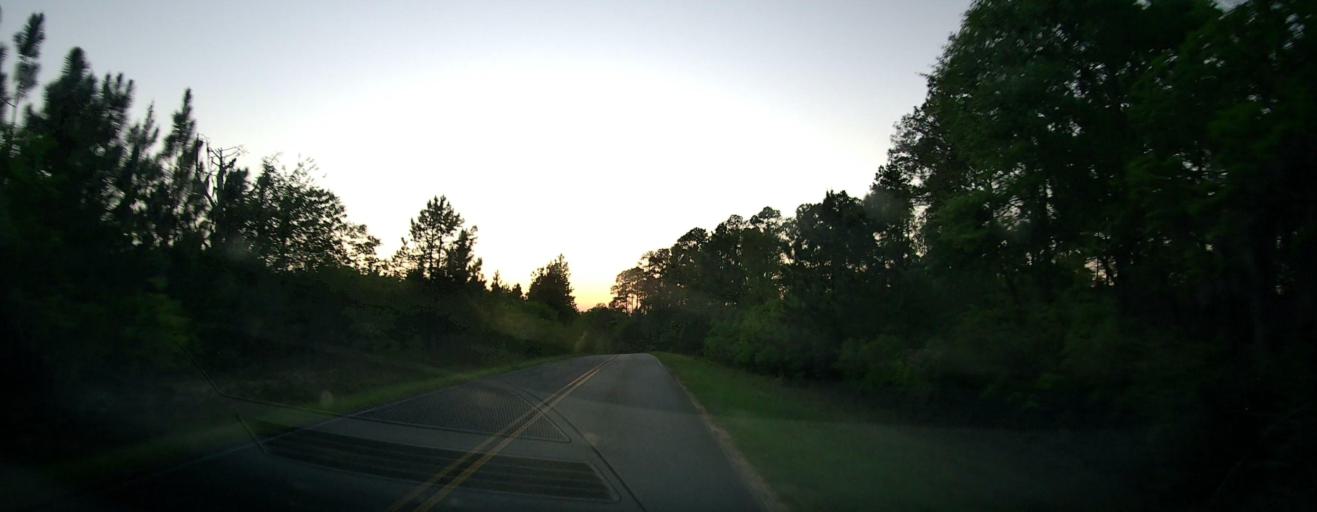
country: US
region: Georgia
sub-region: Marion County
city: Buena Vista
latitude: 32.2549
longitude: -84.6203
